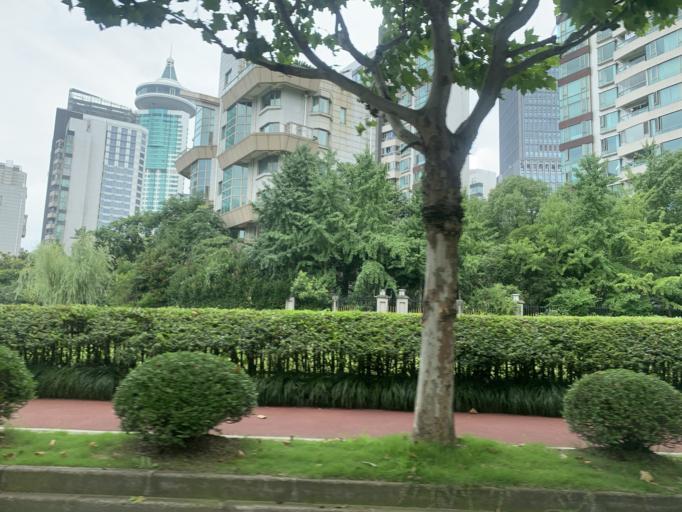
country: CN
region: Shanghai Shi
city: Huamu
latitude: 31.2137
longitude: 121.5339
